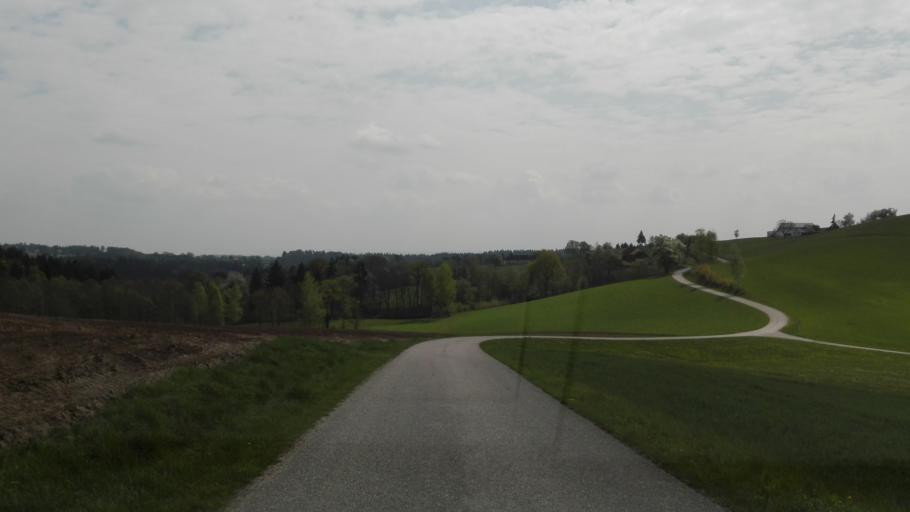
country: AT
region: Upper Austria
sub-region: Politischer Bezirk Perg
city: Perg
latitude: 48.2617
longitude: 14.6883
